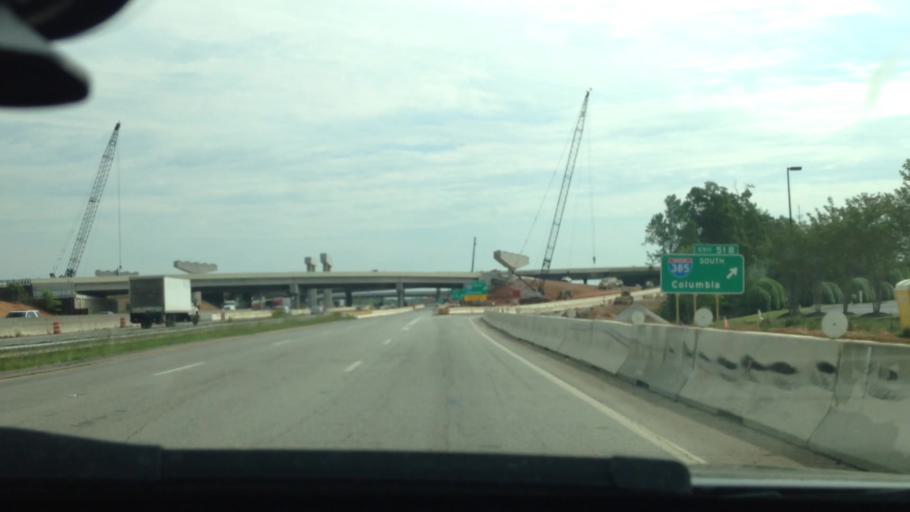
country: US
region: South Carolina
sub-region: Greenville County
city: Mauldin
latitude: 34.8309
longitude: -82.2999
